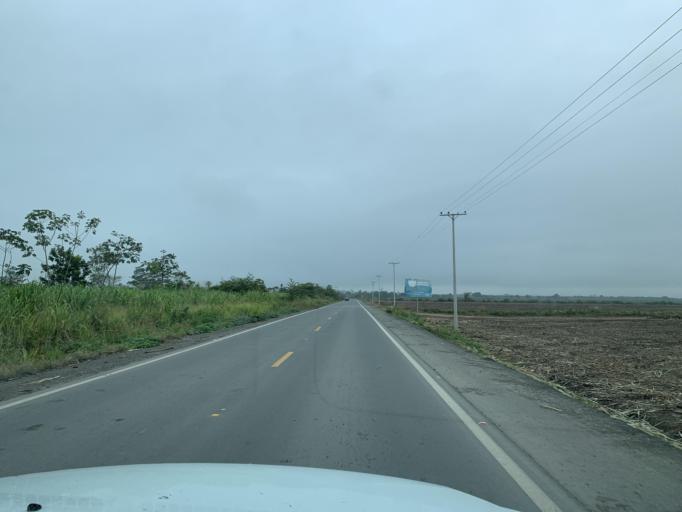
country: EC
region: Guayas
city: Coronel Marcelino Mariduena
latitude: -2.3069
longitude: -79.5061
